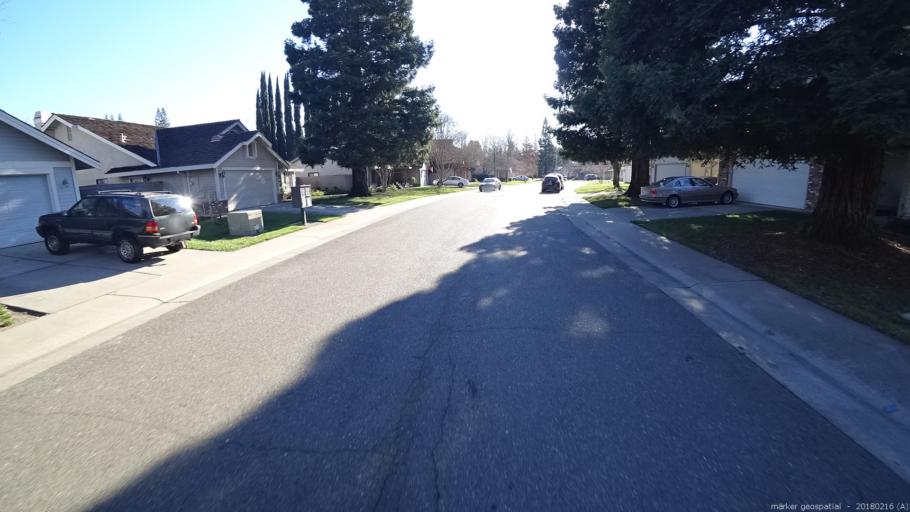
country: US
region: California
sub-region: Sacramento County
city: Gold River
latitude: 38.6268
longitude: -121.2462
